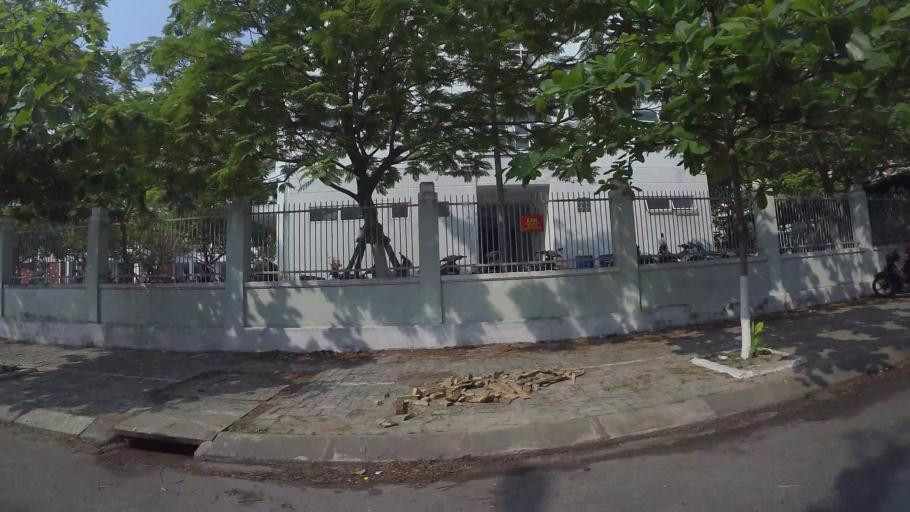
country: VN
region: Da Nang
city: Ngu Hanh Son
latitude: 16.0352
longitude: 108.2430
